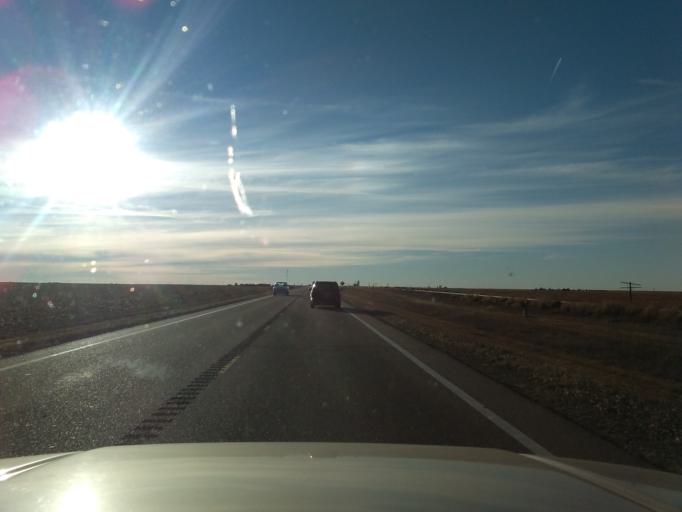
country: US
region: Kansas
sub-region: Thomas County
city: Colby
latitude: 39.4615
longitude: -100.7728
